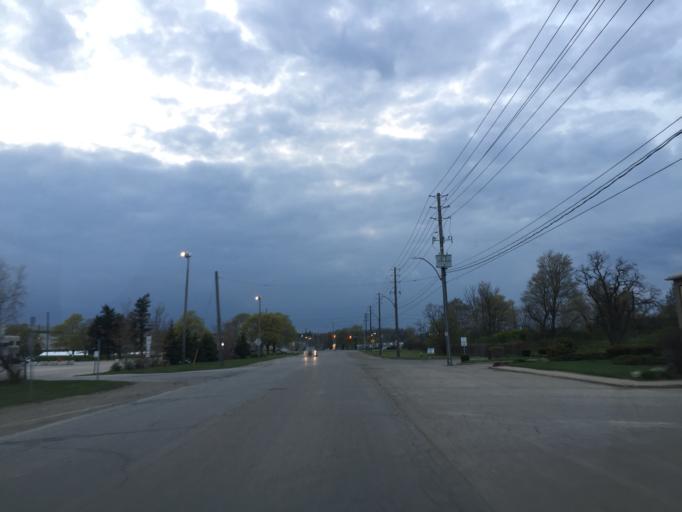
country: CA
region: Ontario
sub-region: Wellington County
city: Guelph
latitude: 43.5553
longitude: -80.2871
